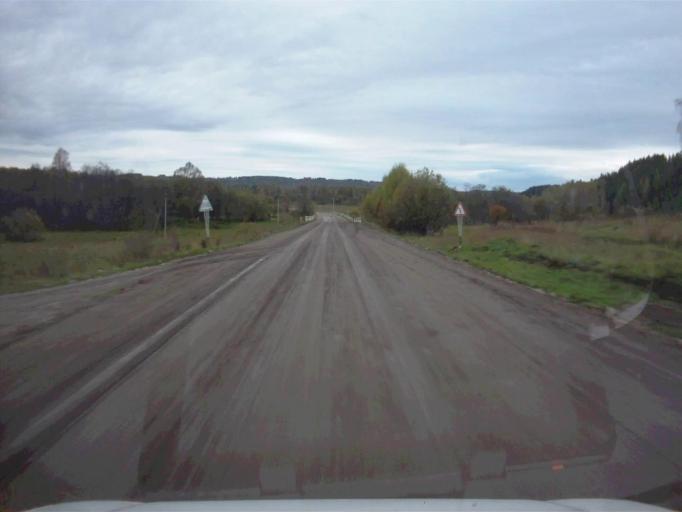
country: RU
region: Chelyabinsk
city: Nyazepetrovsk
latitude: 56.1237
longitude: 59.3569
